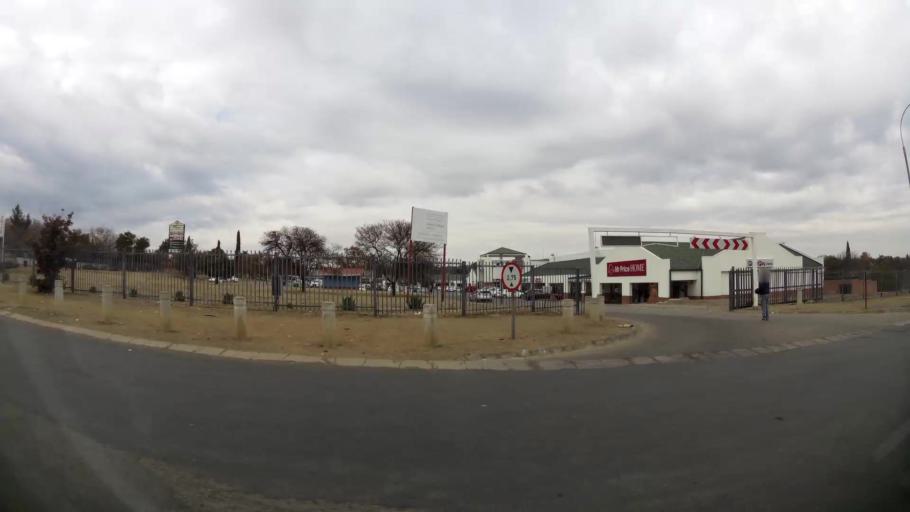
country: ZA
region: Orange Free State
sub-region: Fezile Dabi District Municipality
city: Kroonstad
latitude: -27.6765
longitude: 27.2392
